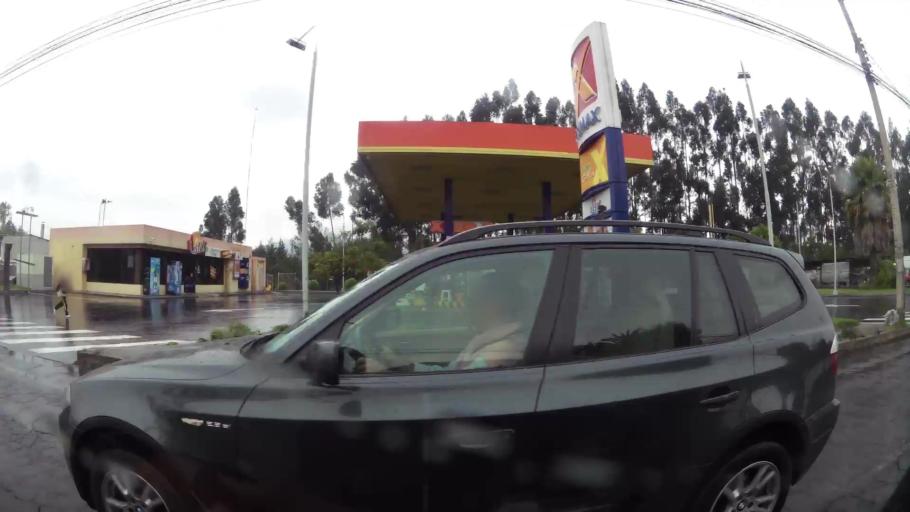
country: EC
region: Pichincha
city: Sangolqui
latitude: -0.3082
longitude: -78.4461
